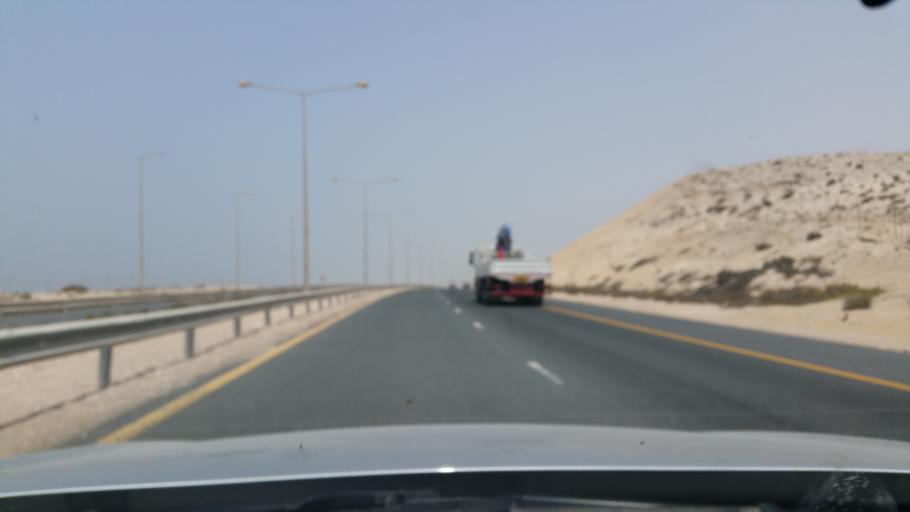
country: QA
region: Baladiyat ar Rayyan
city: Dukhan
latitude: 25.3544
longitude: 50.7799
